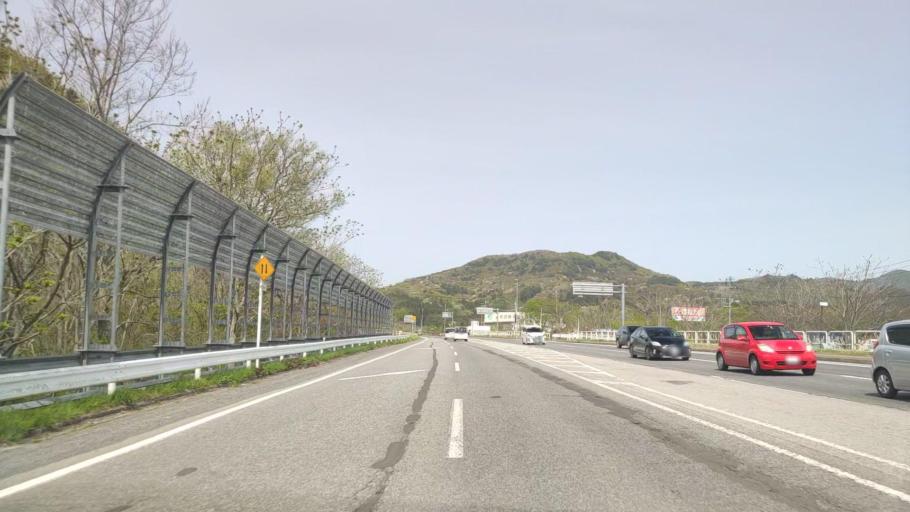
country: JP
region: Aomori
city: Aomori Shi
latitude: 40.8466
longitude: 140.8358
